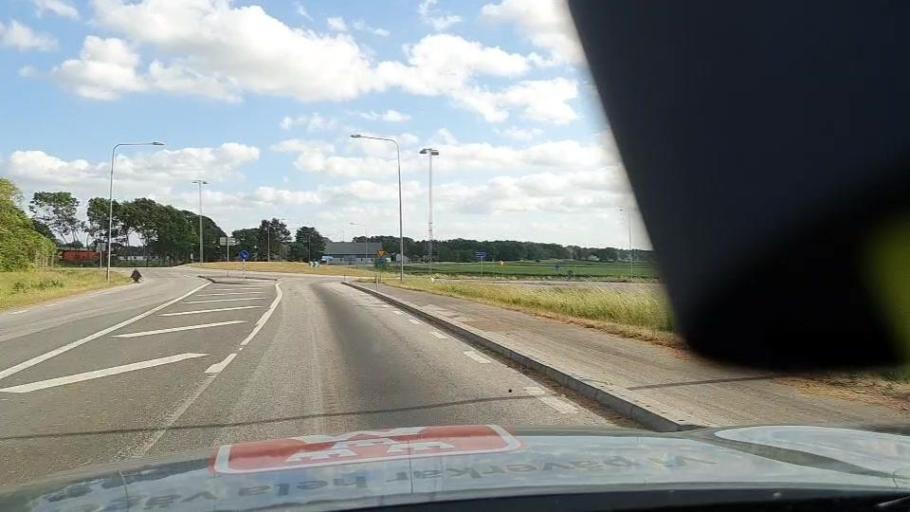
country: SE
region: Blekinge
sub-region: Karlshamns Kommun
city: Morrum
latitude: 56.1127
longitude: 14.6751
